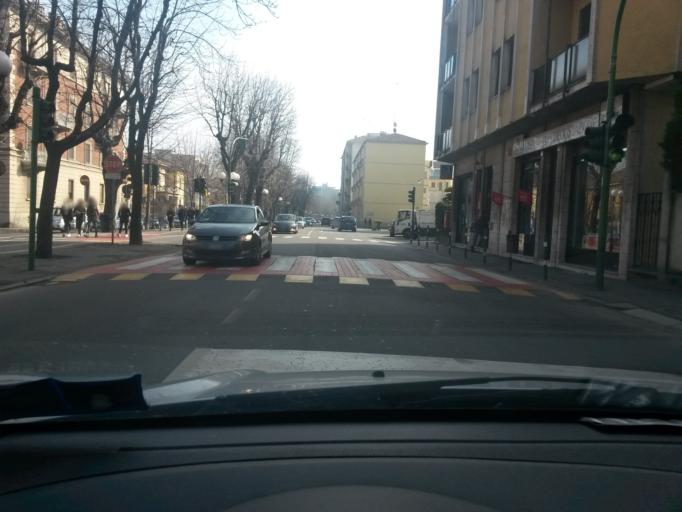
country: IT
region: Piedmont
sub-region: Provincia di Vercelli
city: Vercelli
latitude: 45.3290
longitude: 8.4257
